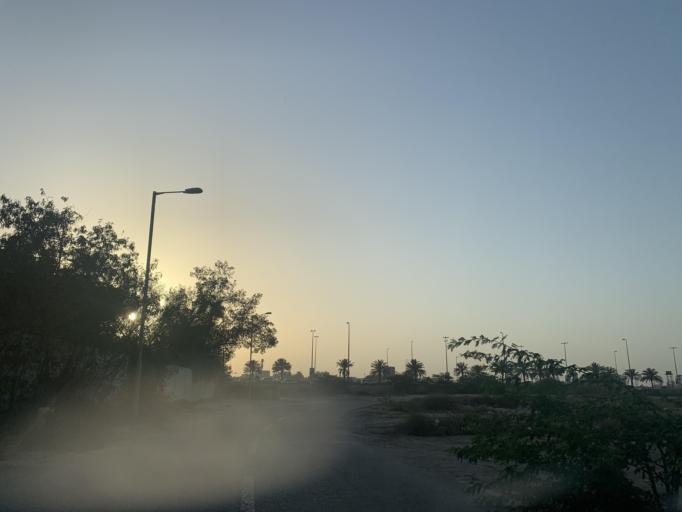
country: BH
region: Manama
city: Jidd Hafs
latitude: 26.2215
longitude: 50.5240
